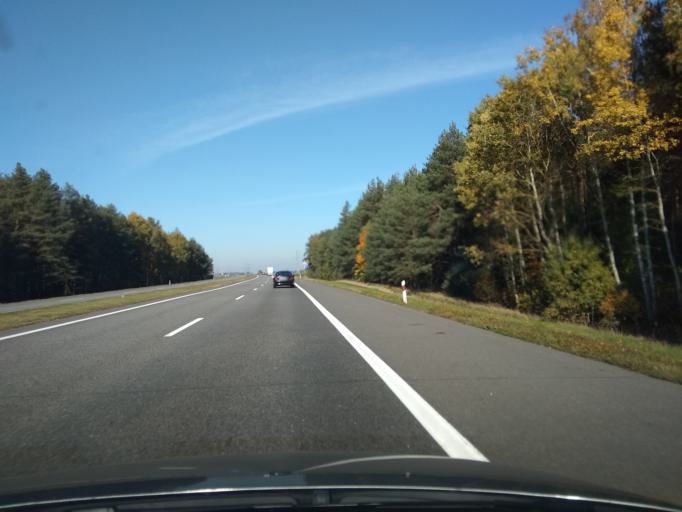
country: BY
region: Brest
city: Baranovichi
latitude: 53.0818
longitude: 25.8865
